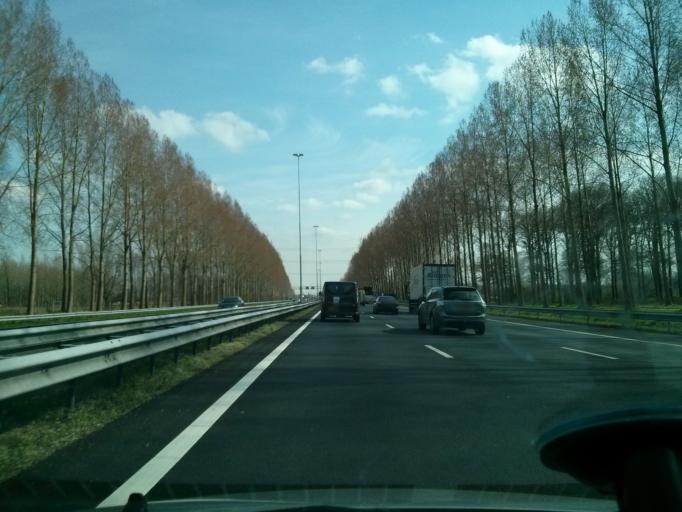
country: NL
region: North Brabant
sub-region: Gemeente Best
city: Best
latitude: 51.5320
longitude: 5.3844
